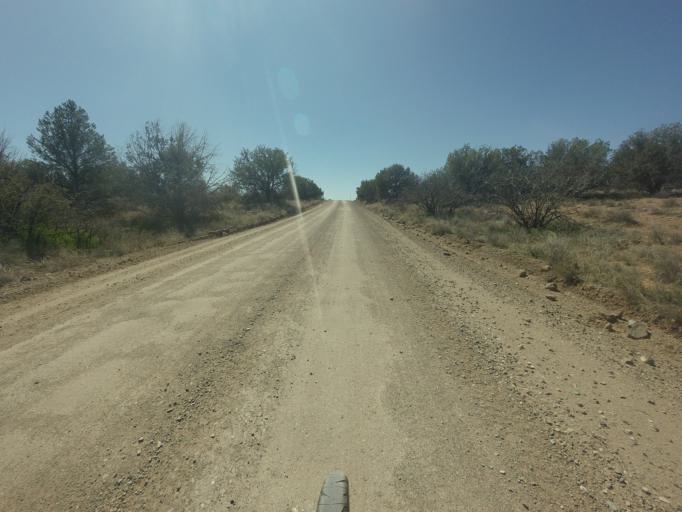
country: US
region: Arizona
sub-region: Yavapai County
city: Lake Montezuma
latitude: 34.6360
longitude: -111.7185
